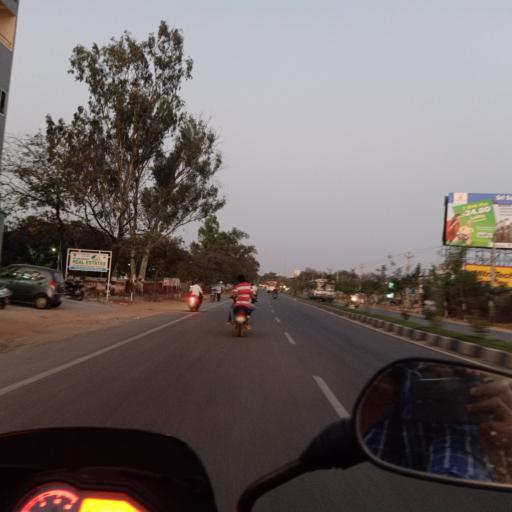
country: IN
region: Telangana
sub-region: Rangareddi
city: Secunderabad
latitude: 17.5612
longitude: 78.5467
